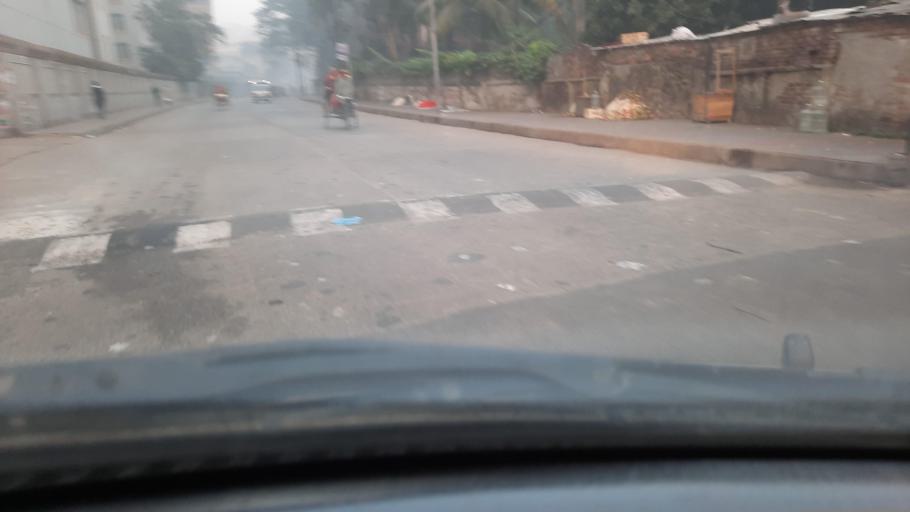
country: BD
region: Dhaka
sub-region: Dhaka
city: Dhaka
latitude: 23.7240
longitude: 90.4024
